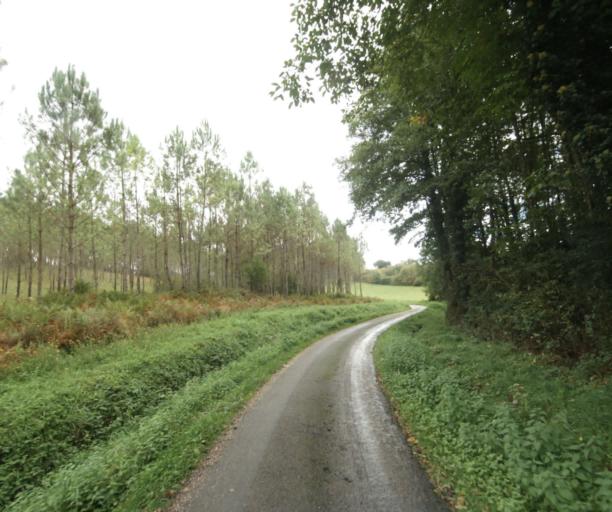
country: FR
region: Midi-Pyrenees
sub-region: Departement du Gers
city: Nogaro
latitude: 43.8232
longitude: -0.0806
